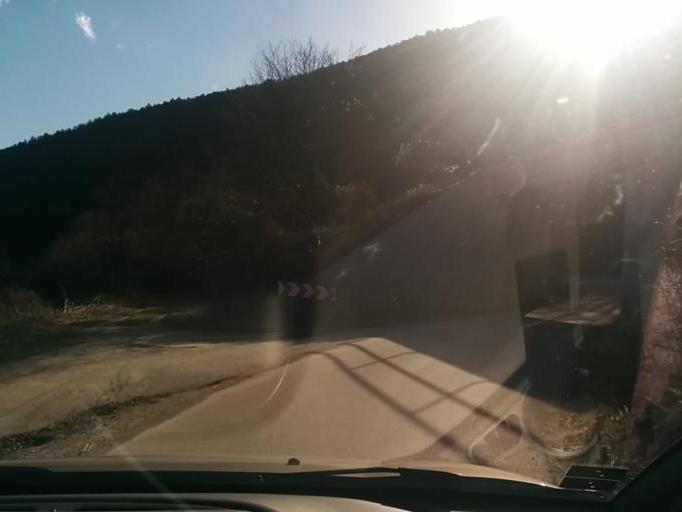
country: SK
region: Nitriansky
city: Cachtice
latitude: 48.7297
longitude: 17.7754
